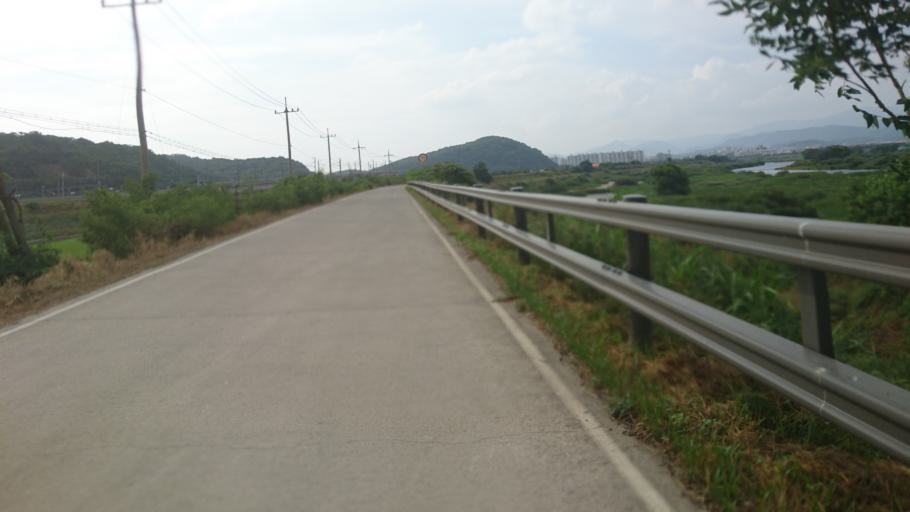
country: KR
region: Gyeongsangbuk-do
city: Gyeongsan-si
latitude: 35.8598
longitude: 128.6799
